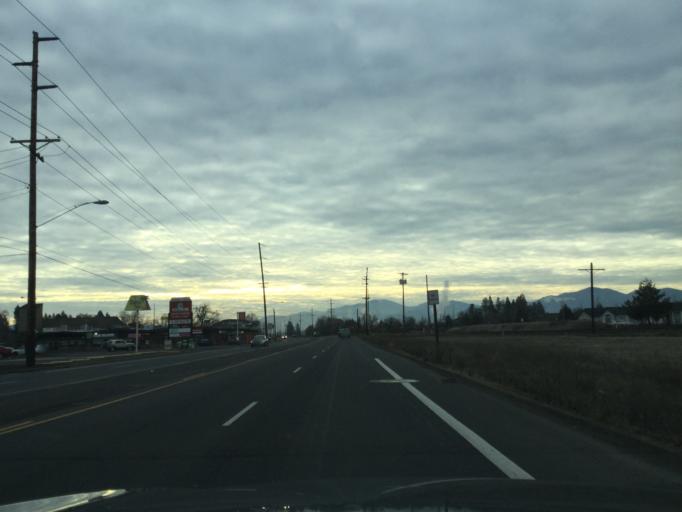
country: US
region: Oregon
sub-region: Jackson County
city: Central Point
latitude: 42.3701
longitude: -122.9147
